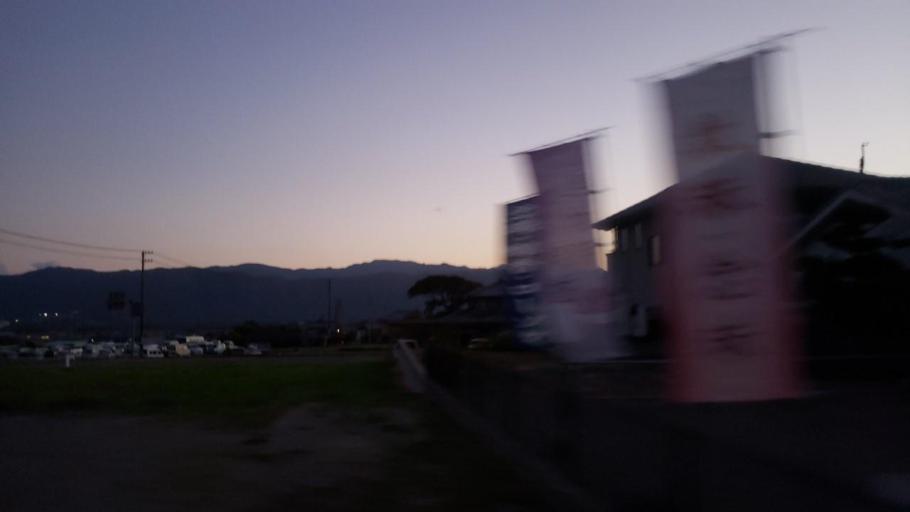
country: JP
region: Tokushima
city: Kamojimacho-jogejima
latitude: 34.1014
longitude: 134.3038
